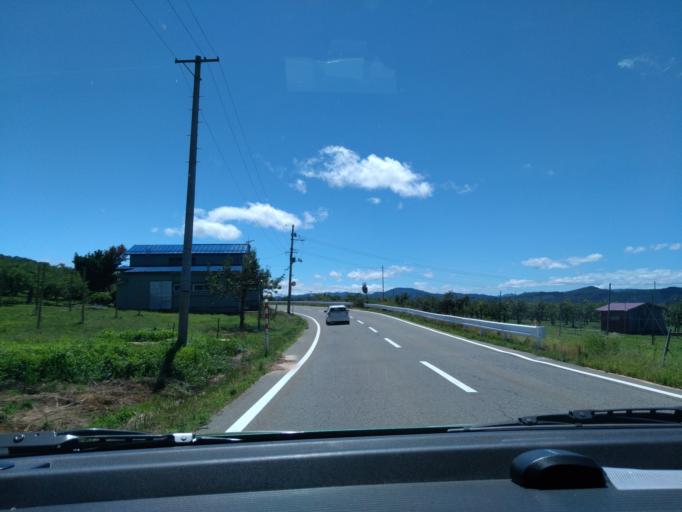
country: JP
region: Akita
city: Yokotemachi
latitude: 39.2368
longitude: 140.5632
